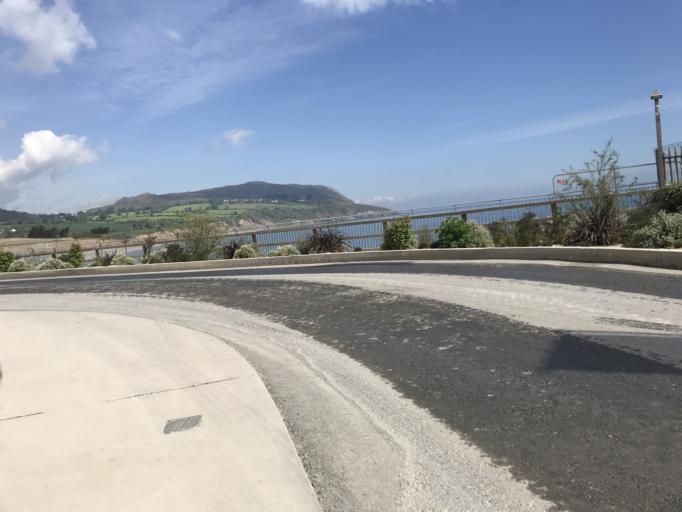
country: IE
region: Leinster
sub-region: Wicklow
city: Greystones
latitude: 53.1539
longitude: -6.0694
